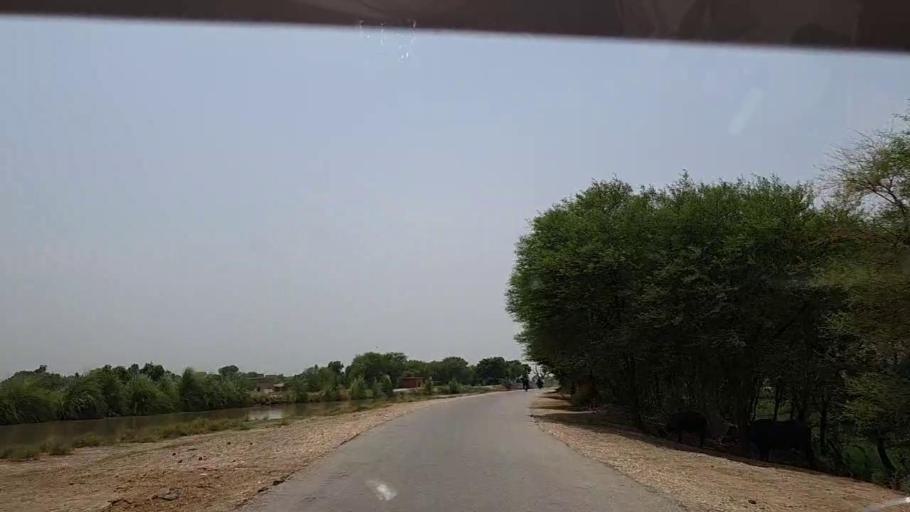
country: PK
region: Sindh
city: Khairpur Nathan Shah
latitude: 27.0066
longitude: 67.6733
